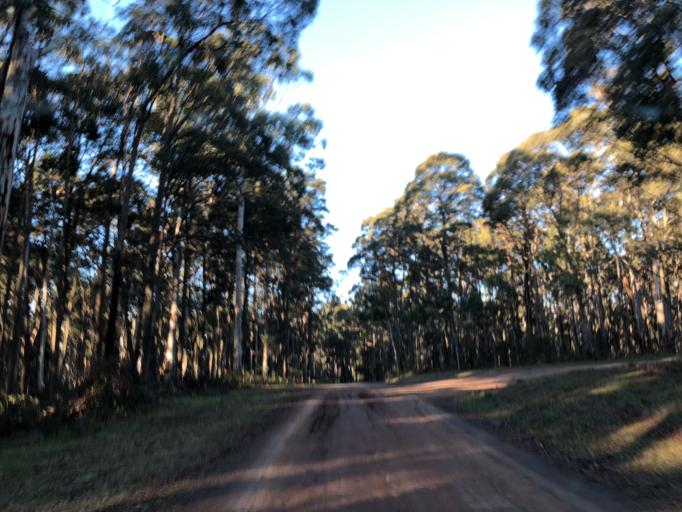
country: AU
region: Victoria
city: Brown Hill
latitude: -37.4770
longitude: 144.1649
